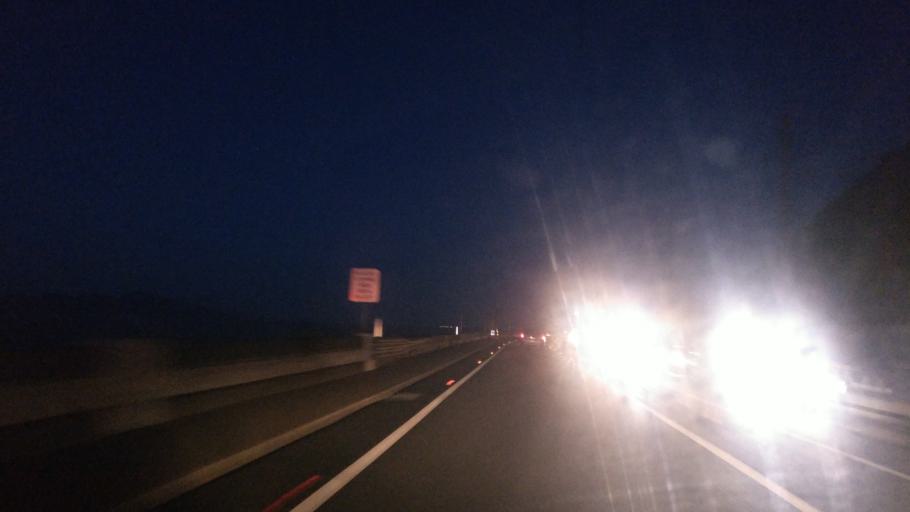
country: NZ
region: Wellington
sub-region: Kapiti Coast District
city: Paraparaumu
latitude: -41.0069
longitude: 174.9264
